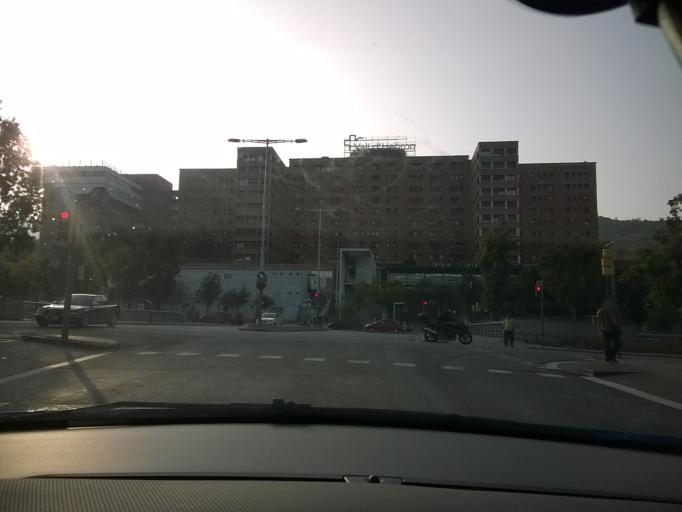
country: ES
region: Catalonia
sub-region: Provincia de Barcelona
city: Horta-Guinardo
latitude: 41.4274
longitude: 2.1442
